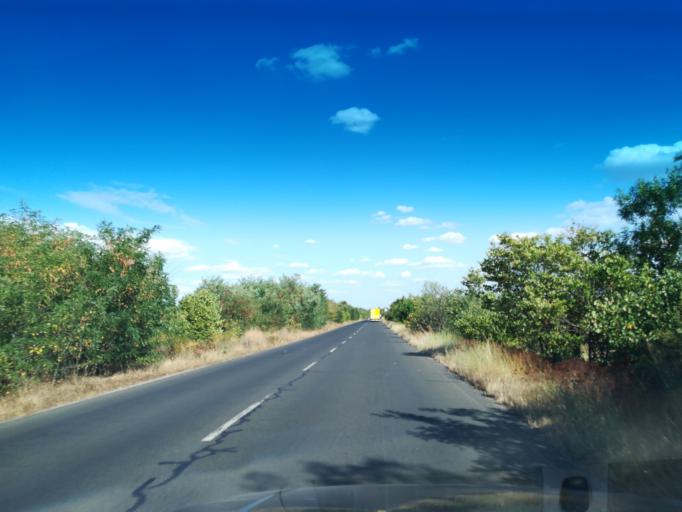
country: BG
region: Khaskovo
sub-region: Obshtina Mineralni Bani
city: Mineralni Bani
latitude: 42.0555
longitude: 25.3030
